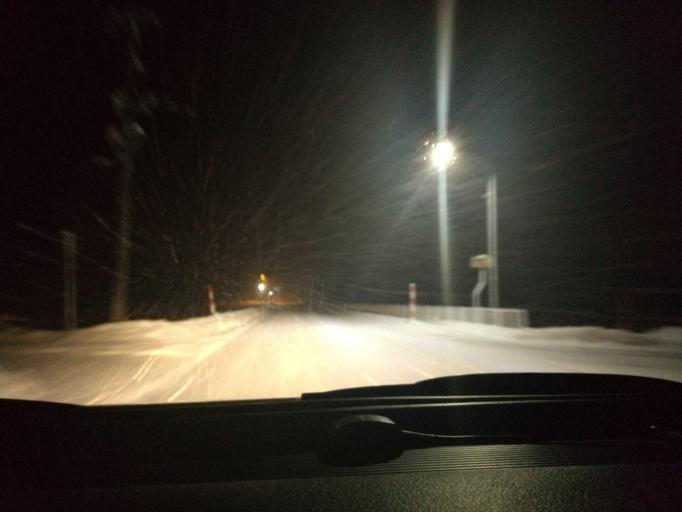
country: JP
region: Akita
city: Kakunodatemachi
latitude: 39.5976
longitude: 140.6176
